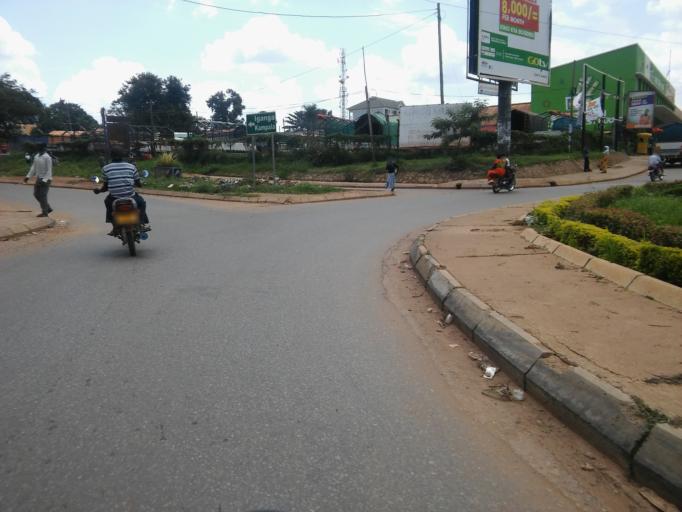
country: UG
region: Eastern Region
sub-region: Mbale District
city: Mbale
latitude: 1.0711
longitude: 34.1749
